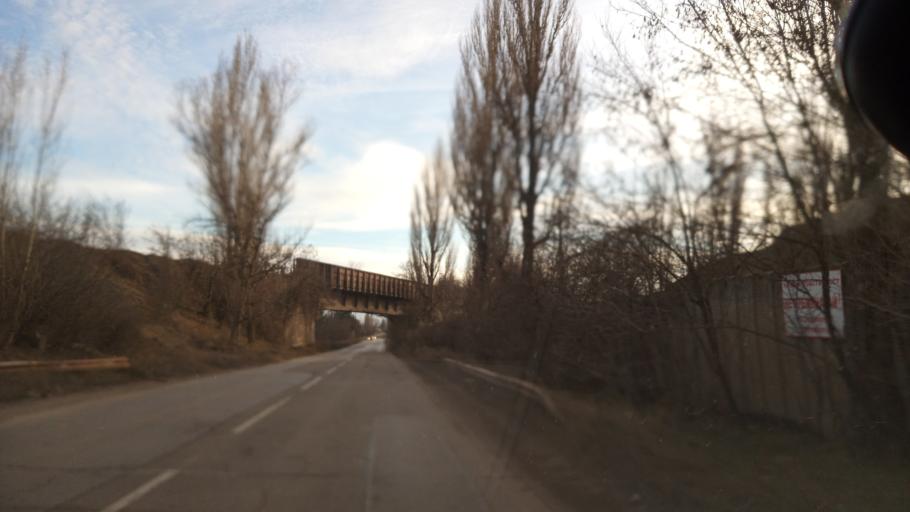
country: BG
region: Sofia-Capital
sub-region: Stolichna Obshtina
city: Bukhovo
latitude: 42.7355
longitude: 23.5538
